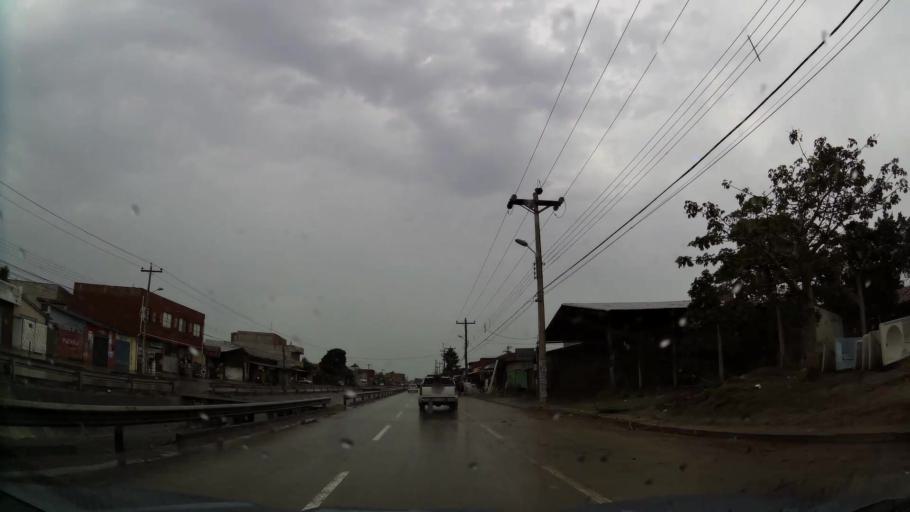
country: BO
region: Santa Cruz
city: Santa Cruz de la Sierra
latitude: -17.8017
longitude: -63.1335
